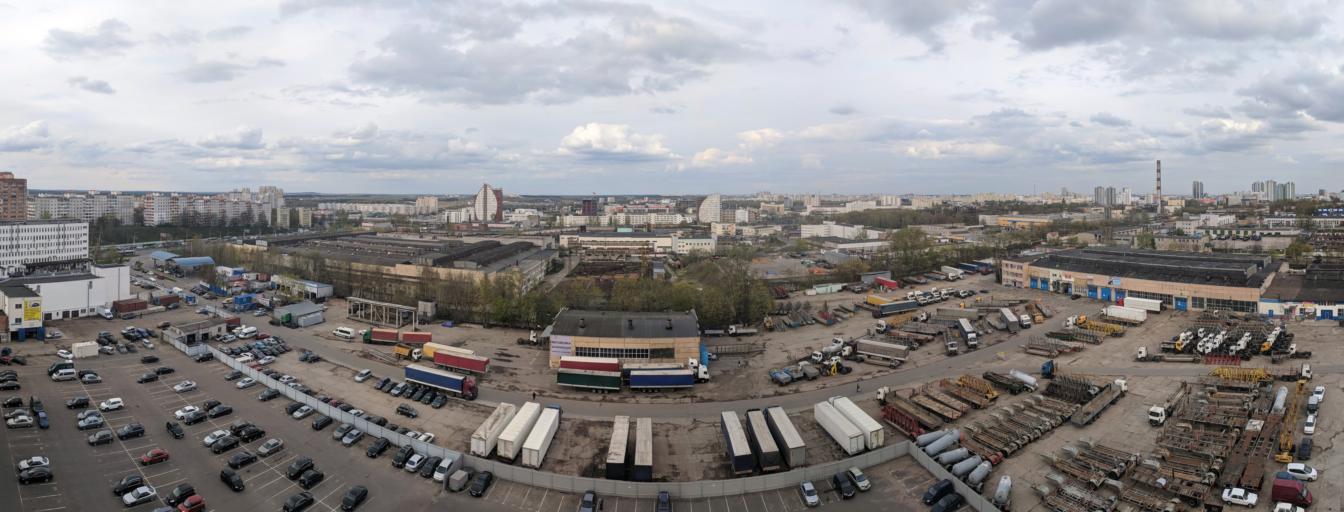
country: BY
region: Minsk
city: Novoye Medvezhino
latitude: 53.9188
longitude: 27.5013
